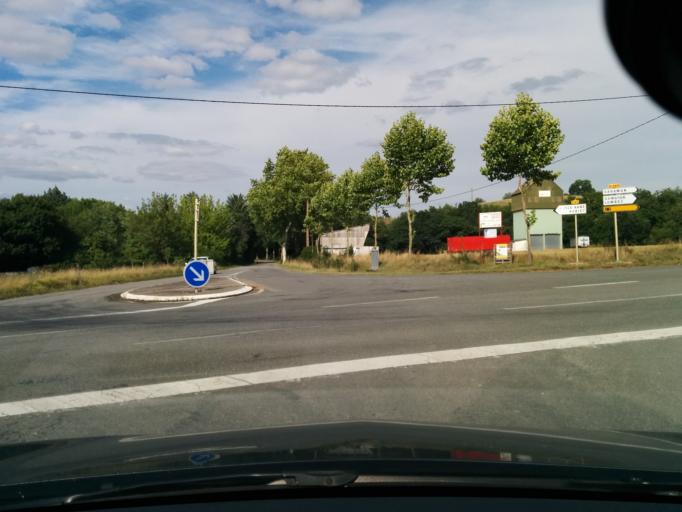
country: FR
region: Midi-Pyrenees
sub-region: Departement du Gers
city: Aubiet
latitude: 43.5866
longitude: 0.7386
